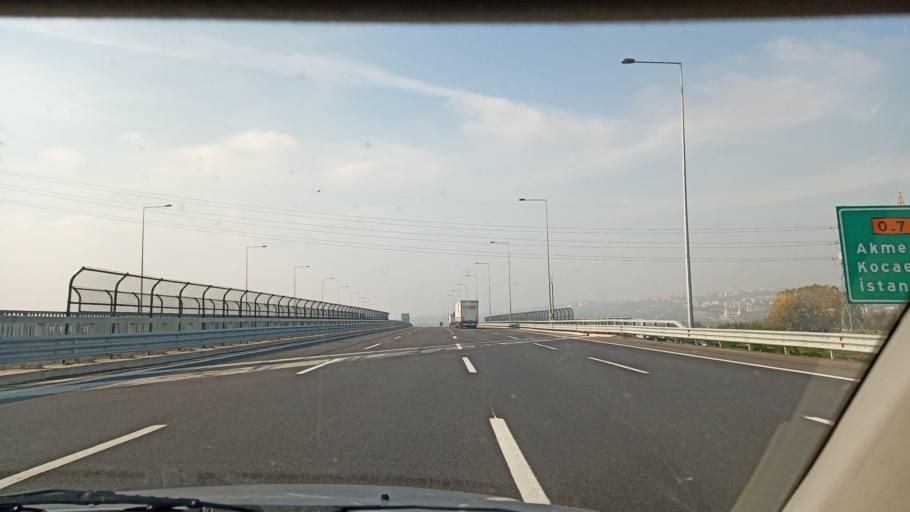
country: TR
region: Sakarya
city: Kazimpasa
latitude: 40.8443
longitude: 30.3326
